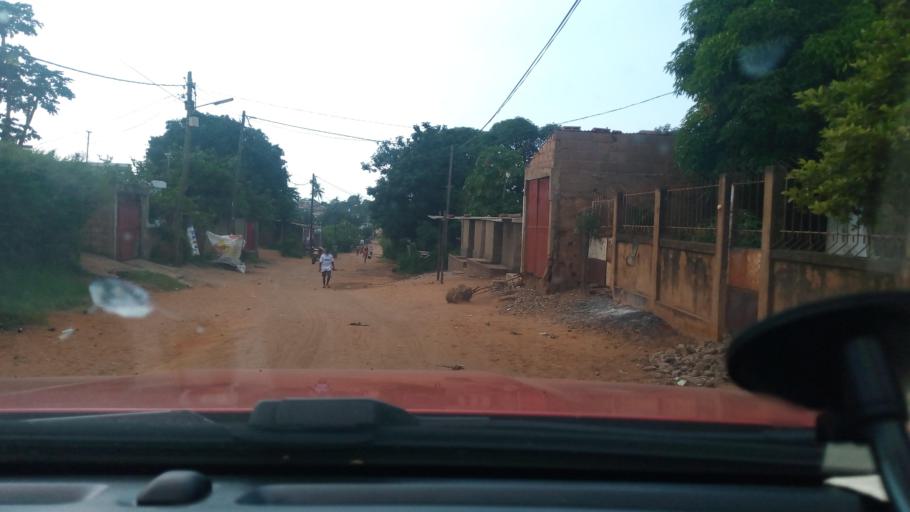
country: MZ
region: Maputo City
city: Maputo
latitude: -25.9214
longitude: 32.5951
